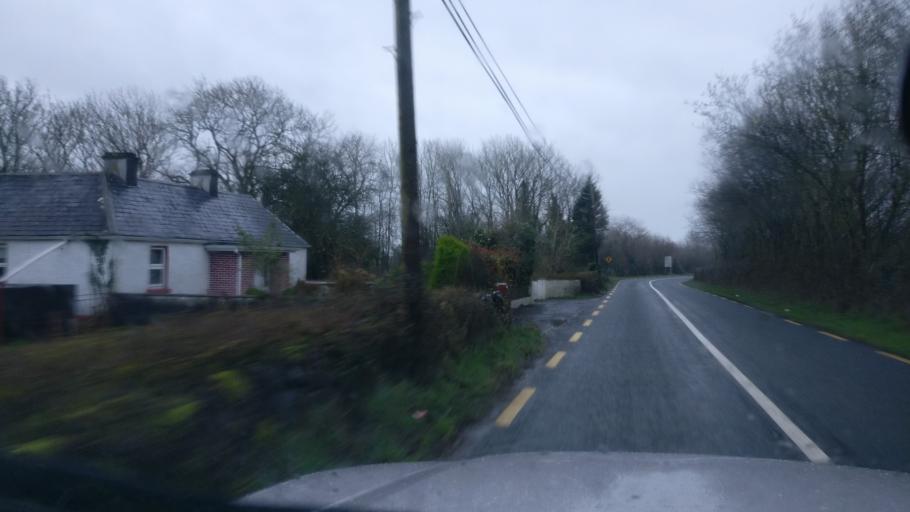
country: IE
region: Connaught
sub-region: County Galway
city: Ballinasloe
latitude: 53.2228
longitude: -8.1940
